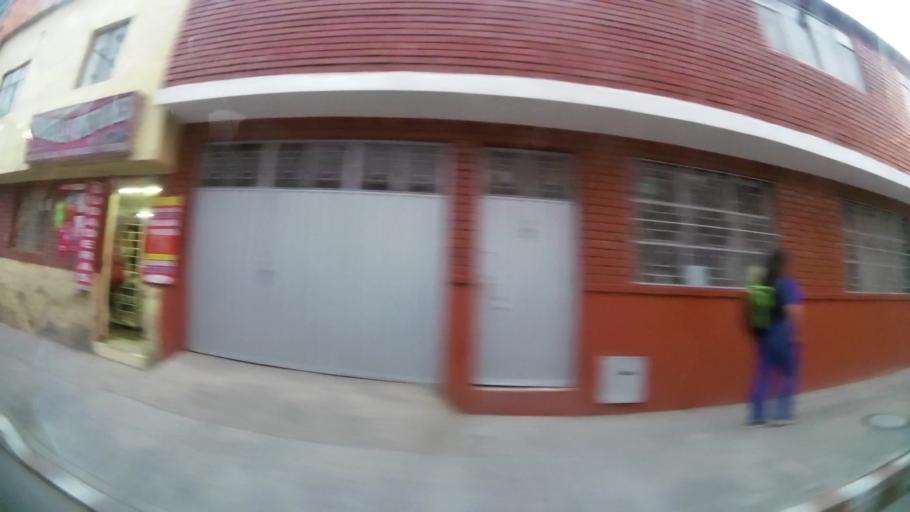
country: CO
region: Bogota D.C.
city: Bogota
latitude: 4.5834
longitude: -74.1372
